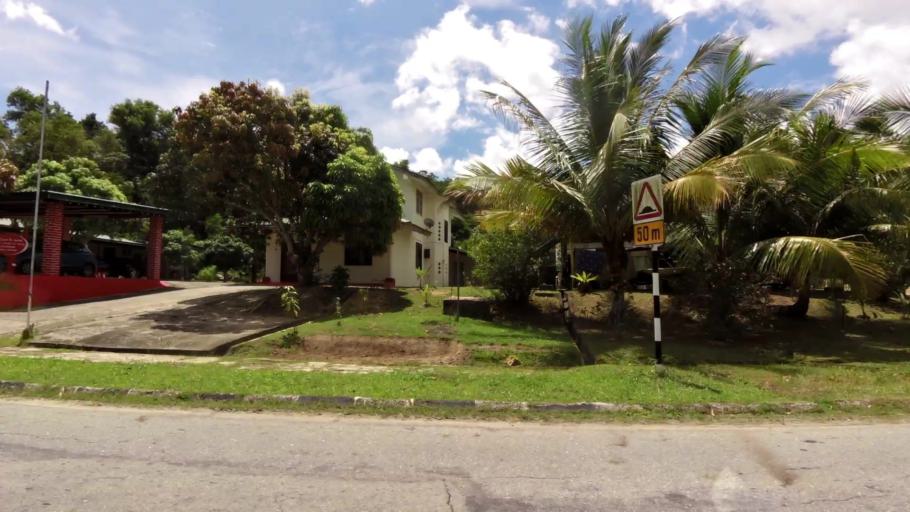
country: BN
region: Brunei and Muara
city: Bandar Seri Begawan
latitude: 4.9577
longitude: 114.9066
